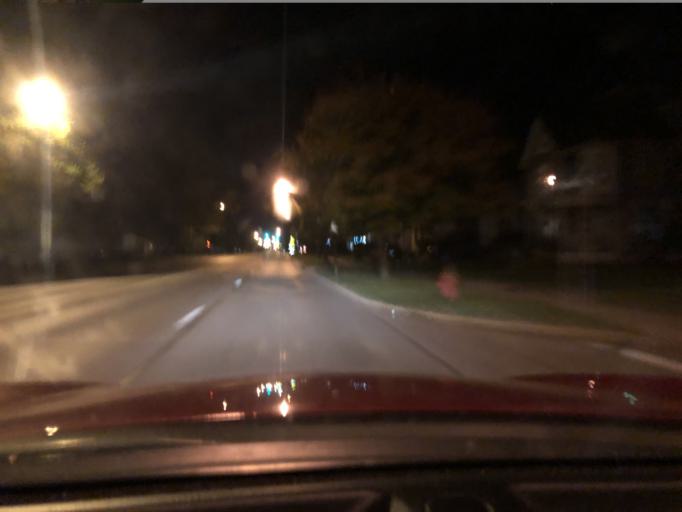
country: US
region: Ohio
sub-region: Logan County
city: Bellefontaine
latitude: 40.3536
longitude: -83.7606
